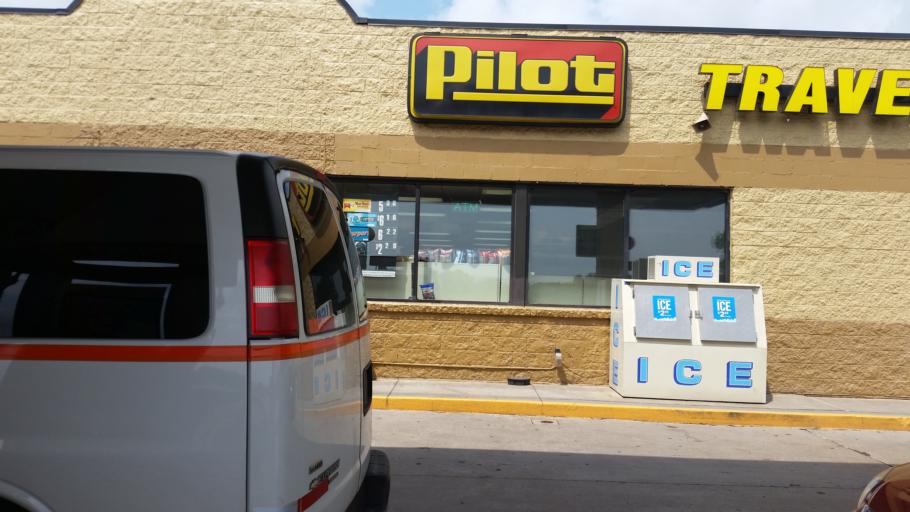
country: US
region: Pennsylvania
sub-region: Luzerne County
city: Conyngham
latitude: 41.0274
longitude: -76.0792
